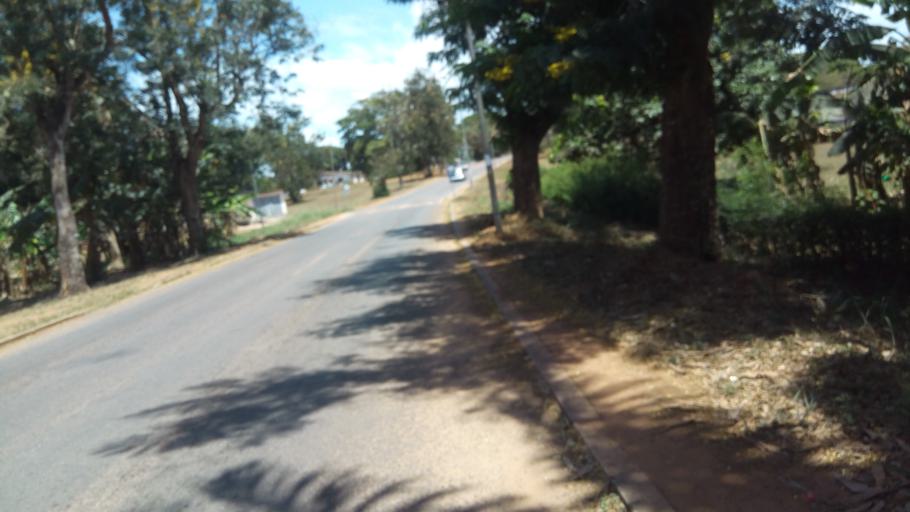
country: GH
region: Central
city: Cape Coast
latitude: 5.1252
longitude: -1.2919
